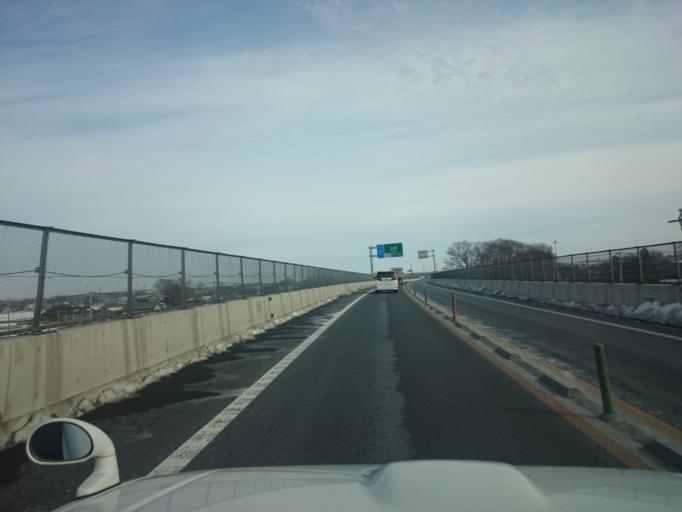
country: JP
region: Saitama
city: Satte
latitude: 36.0835
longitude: 139.7570
